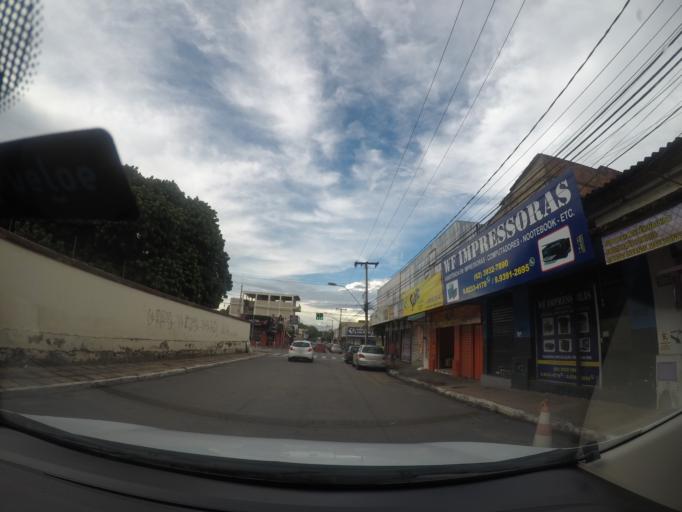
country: BR
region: Goias
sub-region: Goiania
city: Goiania
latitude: -16.6651
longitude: -49.2932
